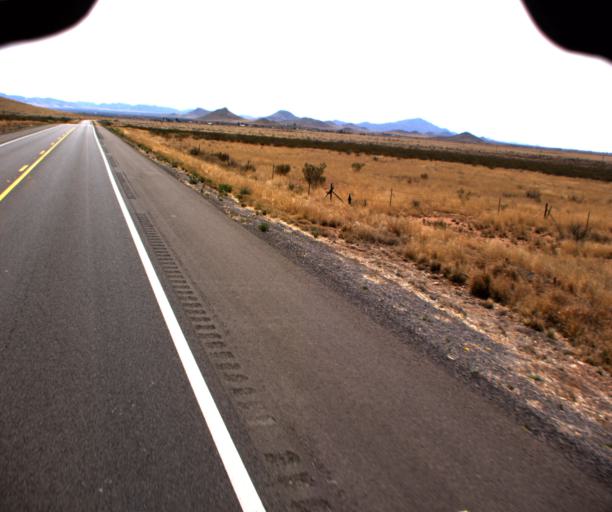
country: US
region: Arizona
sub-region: Cochise County
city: Willcox
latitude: 31.9012
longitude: -109.7102
